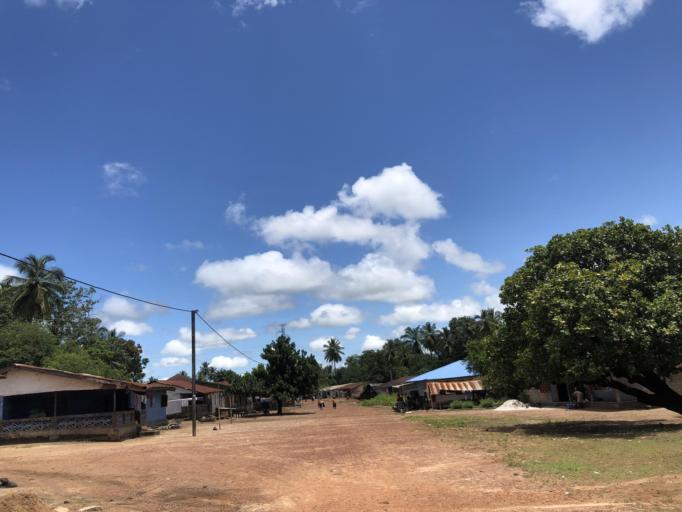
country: SL
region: Northern Province
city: Makeni
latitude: 8.8678
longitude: -12.1254
